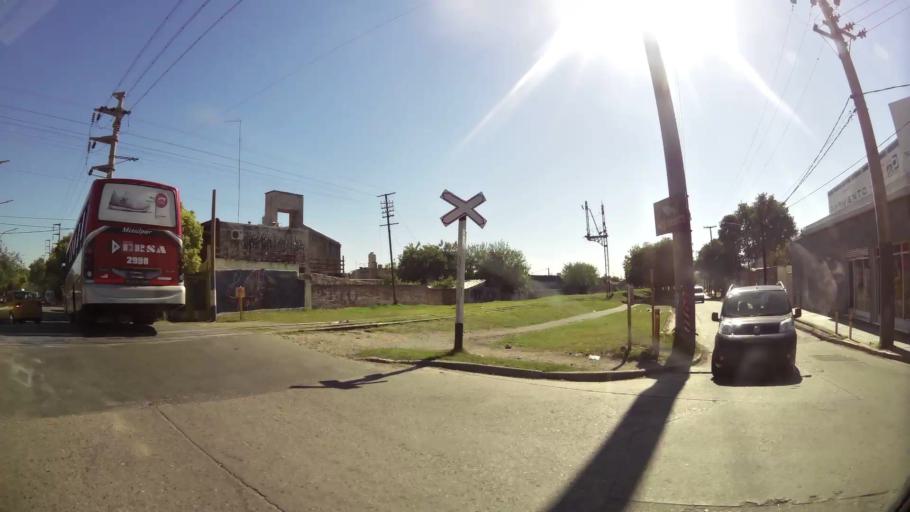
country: AR
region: Cordoba
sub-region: Departamento de Capital
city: Cordoba
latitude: -31.4406
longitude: -64.1687
